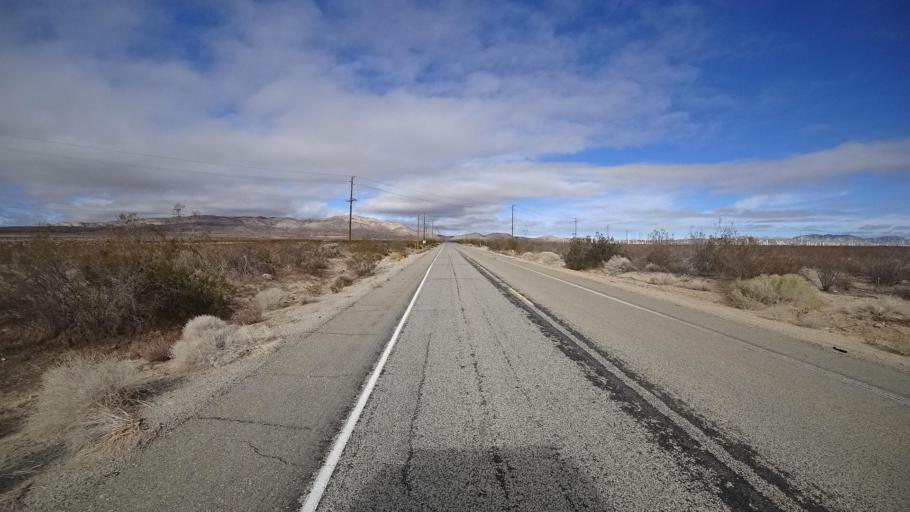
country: US
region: California
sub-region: Kern County
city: Mojave
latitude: 34.9758
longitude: -118.3093
